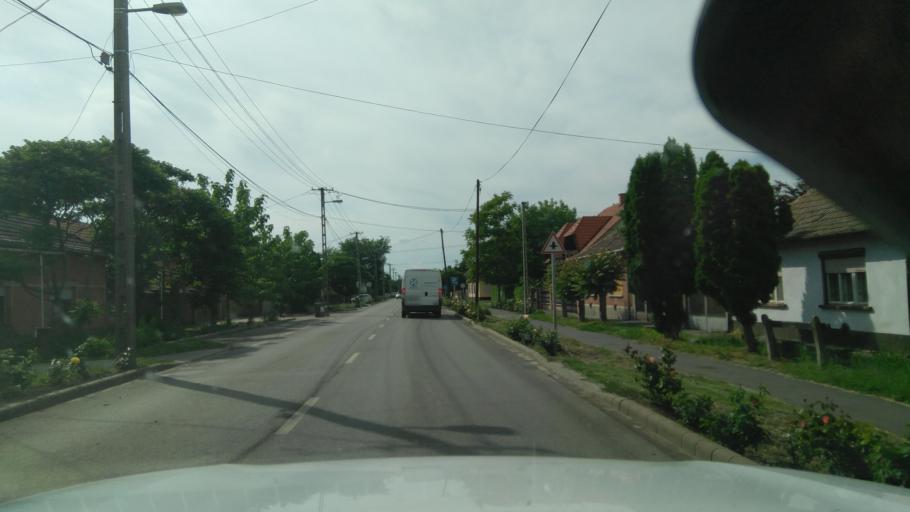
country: HU
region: Bekes
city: Medgyesegyhaza
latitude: 46.5013
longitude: 21.0214
